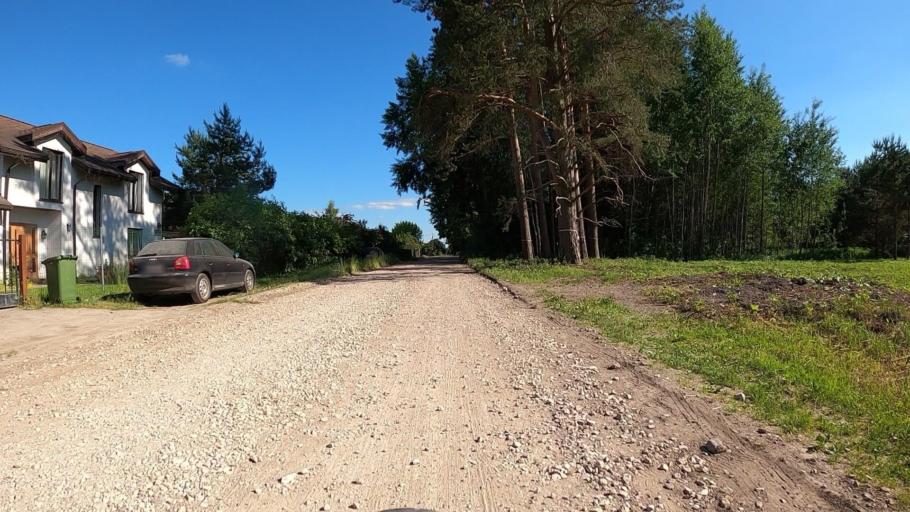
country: LV
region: Stopini
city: Ulbroka
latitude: 56.9096
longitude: 24.3136
